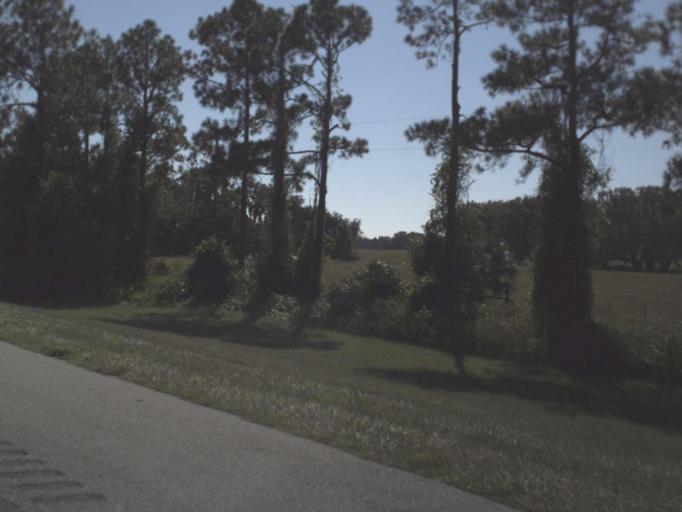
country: US
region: Florida
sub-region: Sumter County
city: Wildwood
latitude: 28.7901
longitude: -81.9890
